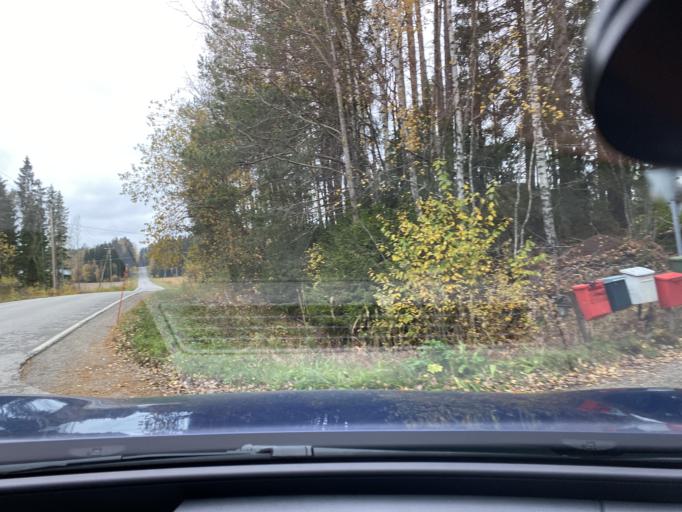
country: FI
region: Varsinais-Suomi
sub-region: Vakka-Suomi
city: Pyhaeranta
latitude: 60.9173
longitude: 21.5680
